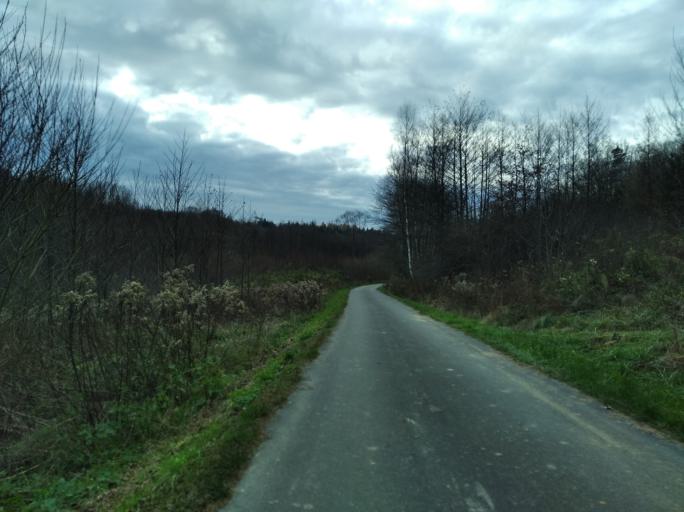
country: PL
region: Subcarpathian Voivodeship
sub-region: Powiat brzozowski
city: Domaradz
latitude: 49.7817
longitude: 21.9333
